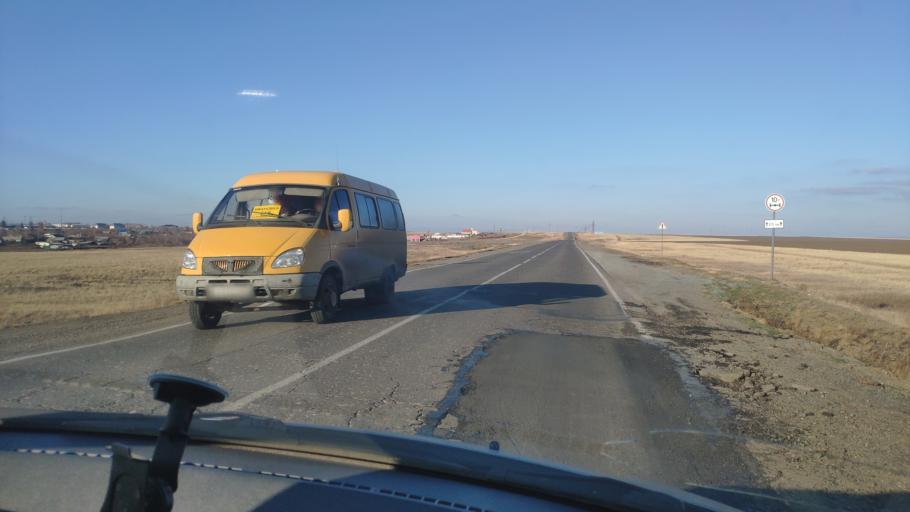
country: RU
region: Orenburg
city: Gay
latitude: 51.6274
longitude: 58.3647
